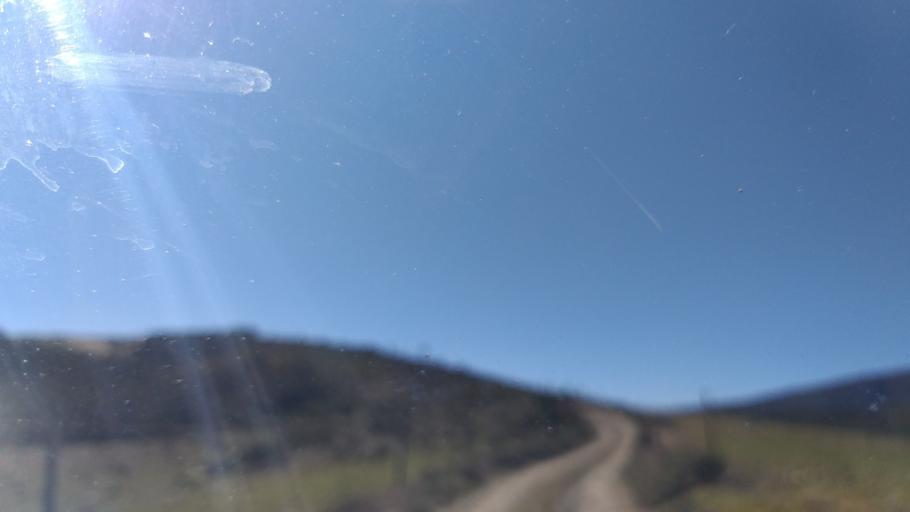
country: PT
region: Guarda
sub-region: Manteigas
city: Manteigas
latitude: 40.4505
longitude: -7.4988
